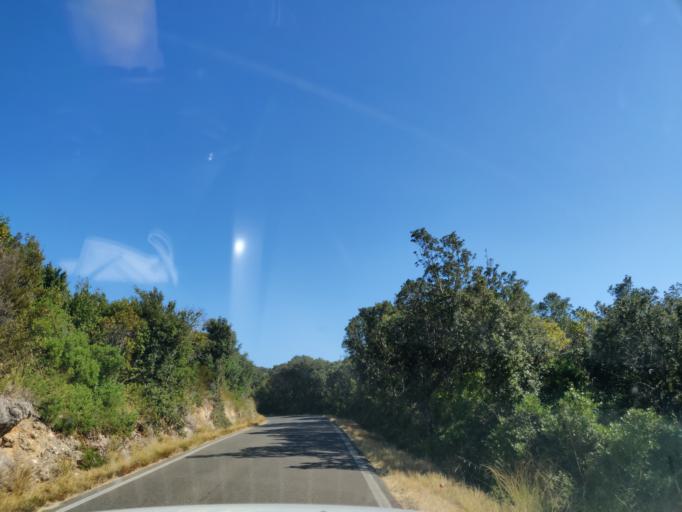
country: IT
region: Tuscany
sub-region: Provincia di Grosseto
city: Porto Ercole
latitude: 42.4282
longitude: 11.1719
